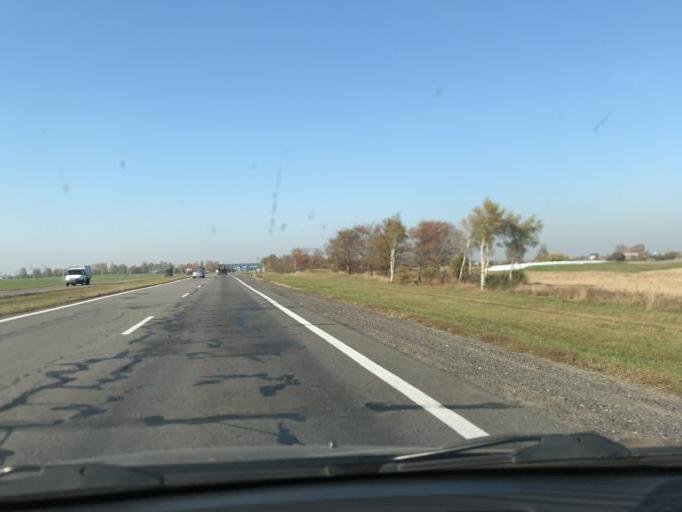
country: BY
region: Minsk
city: Dukora
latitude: 53.7003
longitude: 27.8859
